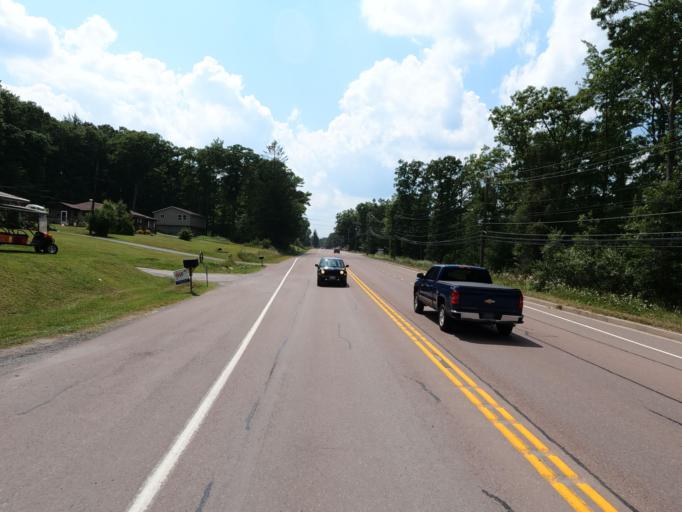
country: US
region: Maryland
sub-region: Garrett County
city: Mountain Lake Park
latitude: 39.4996
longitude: -79.3311
